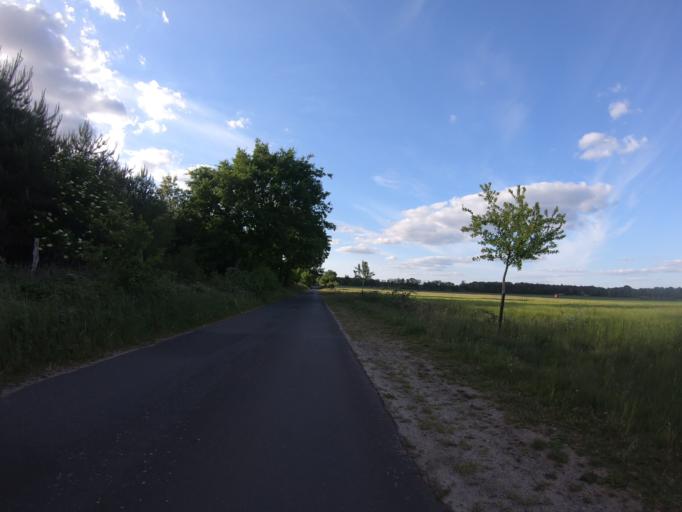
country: DE
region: Lower Saxony
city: Wagenhoff
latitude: 52.5170
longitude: 10.4720
